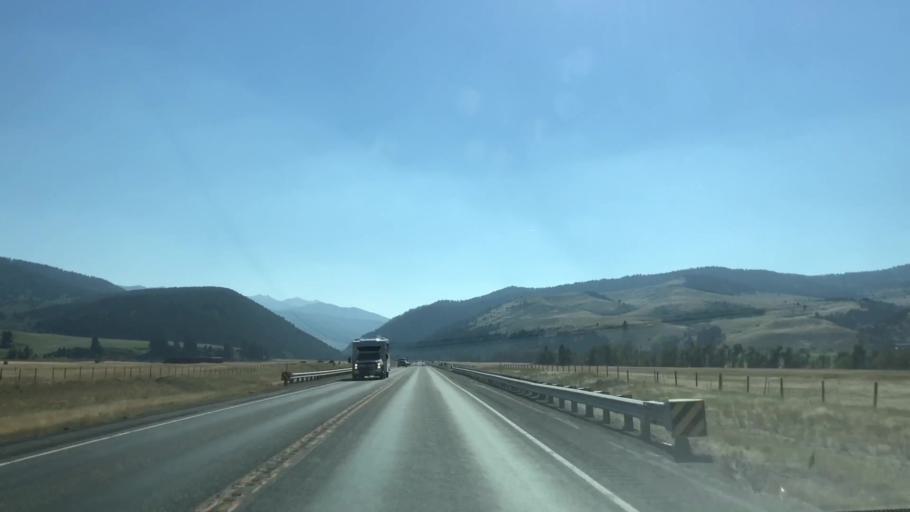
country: US
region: Montana
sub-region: Gallatin County
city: Four Corners
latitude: 45.5346
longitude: -111.2330
